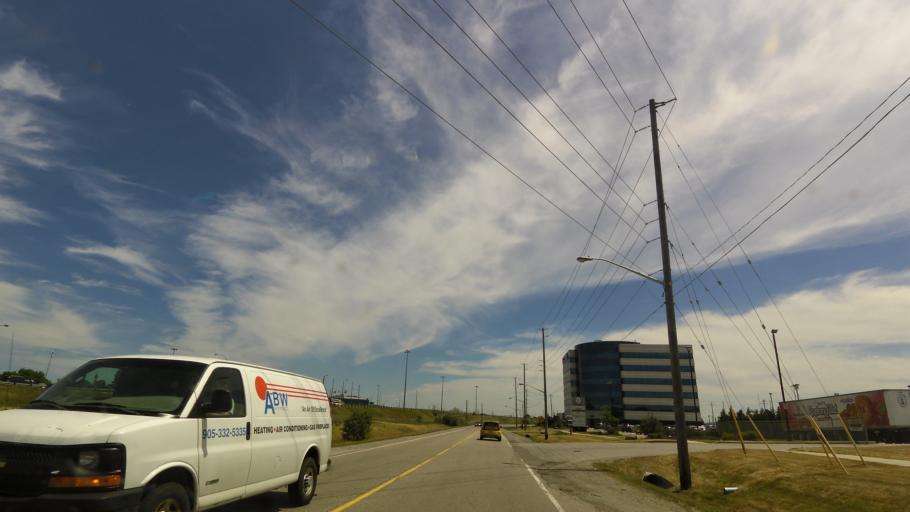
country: CA
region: Ontario
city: Burlington
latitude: 43.3826
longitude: -79.7759
